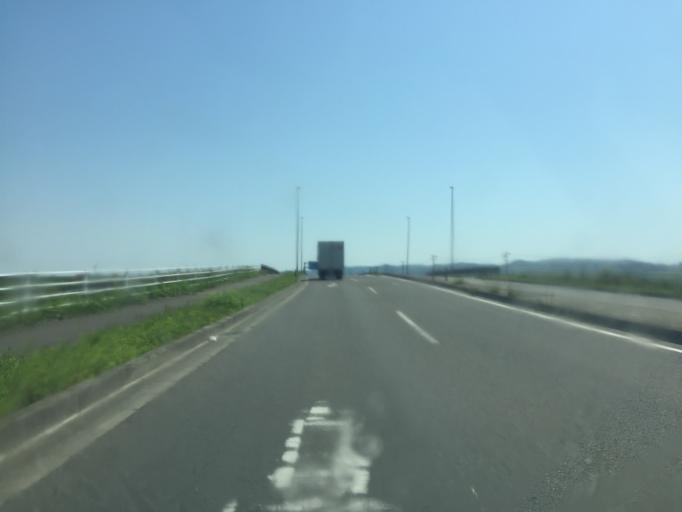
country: JP
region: Miyagi
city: Iwanuma
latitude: 38.1488
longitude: 140.8639
